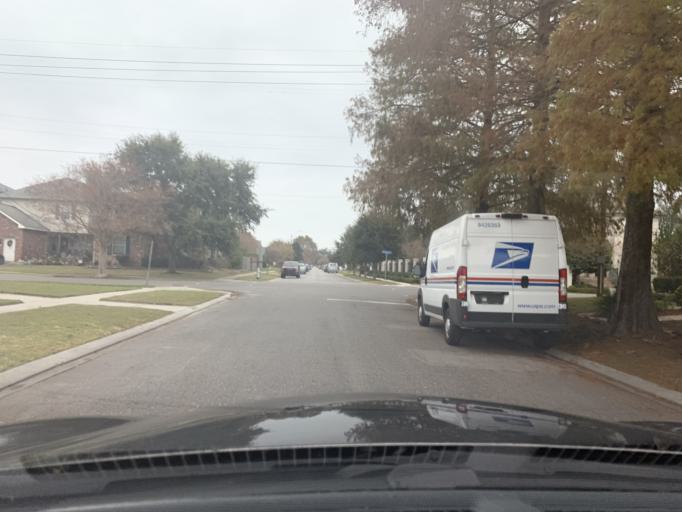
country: US
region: Louisiana
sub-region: Jefferson Parish
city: Metairie
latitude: 30.0119
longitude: -90.1059
